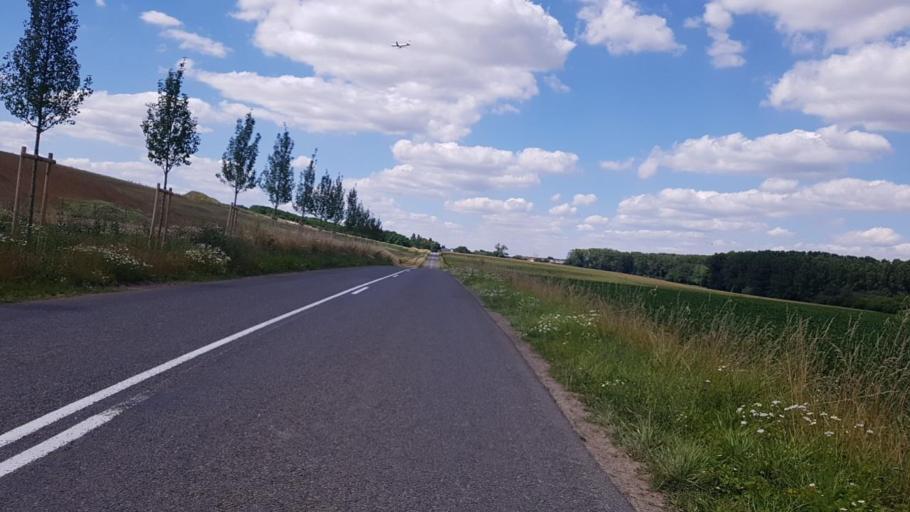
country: FR
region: Ile-de-France
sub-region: Departement de Seine-et-Marne
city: Longperrier
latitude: 49.0221
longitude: 2.6463
